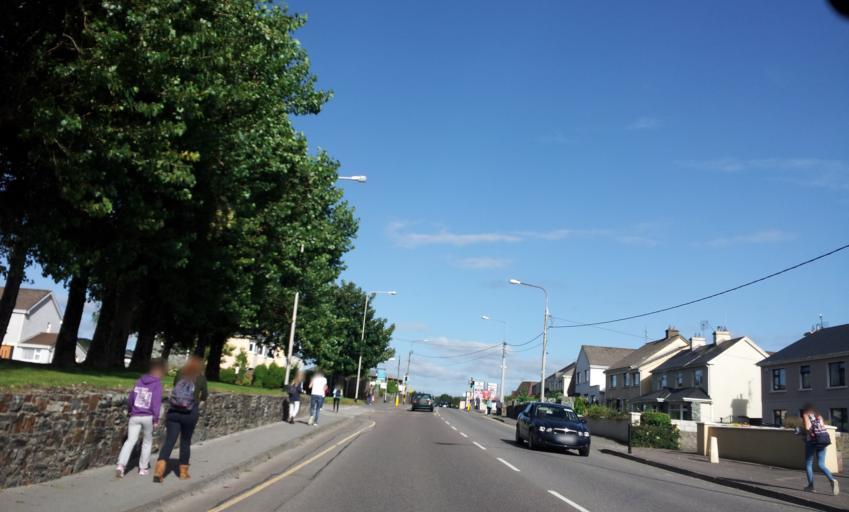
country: IE
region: Munster
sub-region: Ciarrai
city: Cill Airne
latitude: 52.0602
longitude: -9.4966
